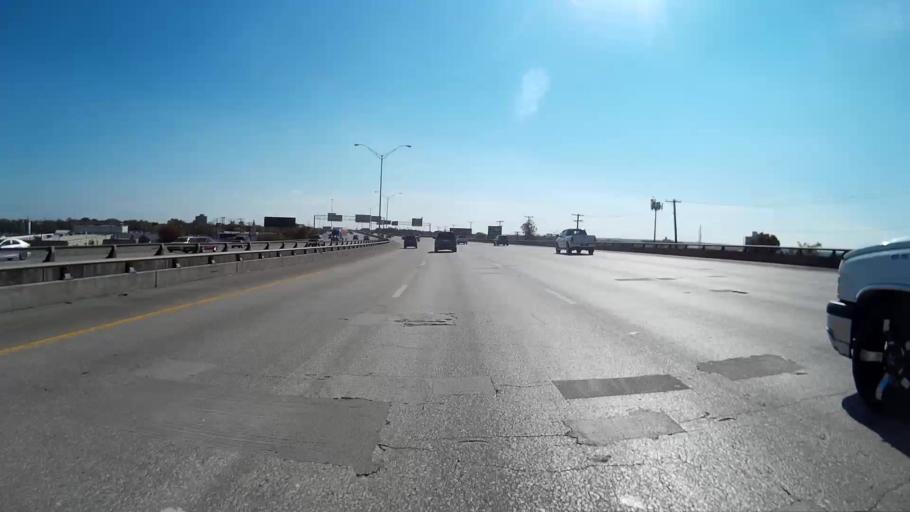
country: US
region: Texas
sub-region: Dallas County
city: Dallas
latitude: 32.7720
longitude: -96.7784
